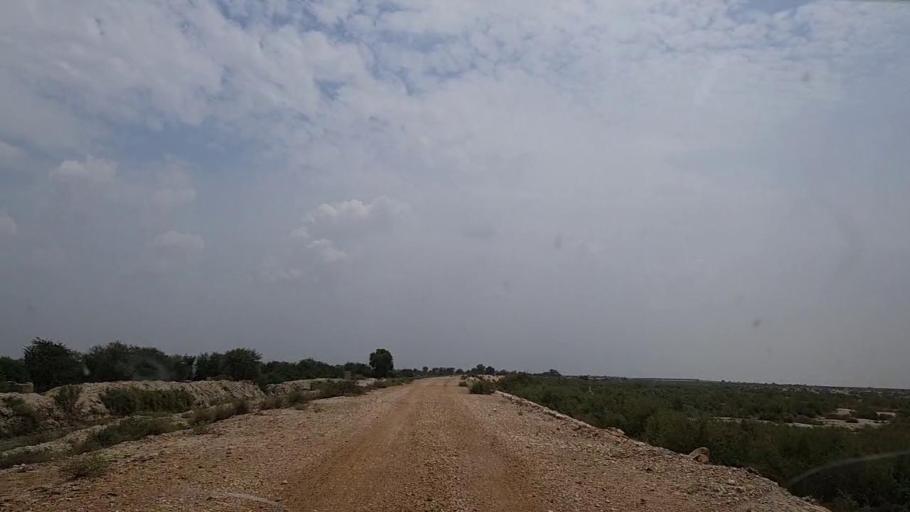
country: PK
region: Sindh
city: Phulji
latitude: 26.8322
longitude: 67.6173
